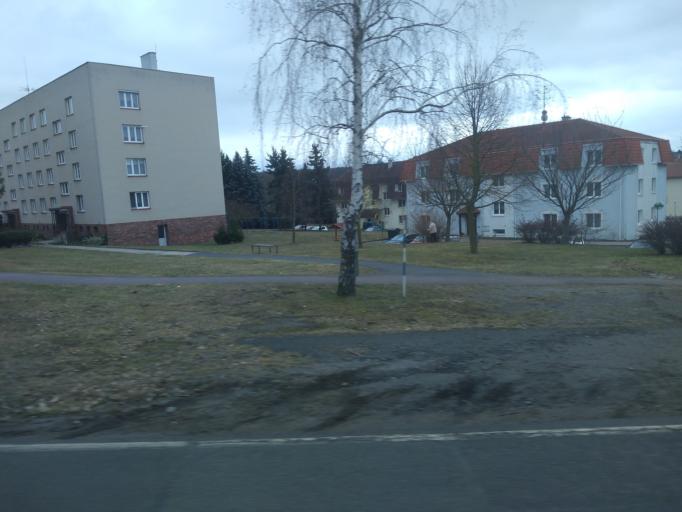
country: CZ
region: Plzensky
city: Vejprnice
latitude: 49.7314
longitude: 13.2781
